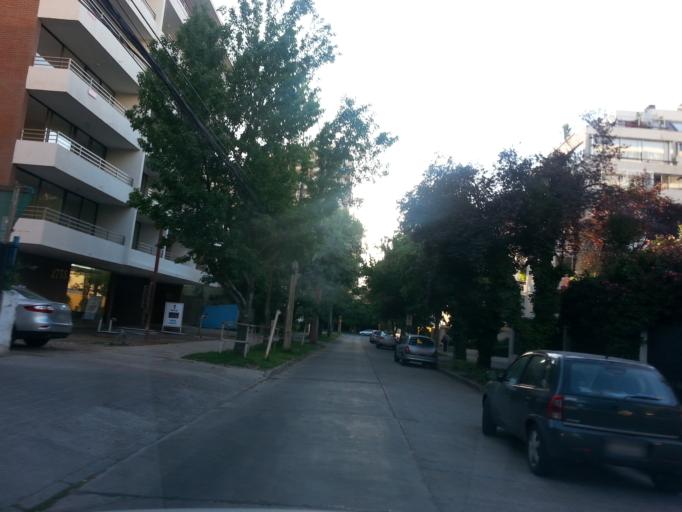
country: CL
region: Santiago Metropolitan
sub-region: Provincia de Santiago
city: Villa Presidente Frei, Nunoa, Santiago, Chile
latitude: -33.4294
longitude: -70.5961
